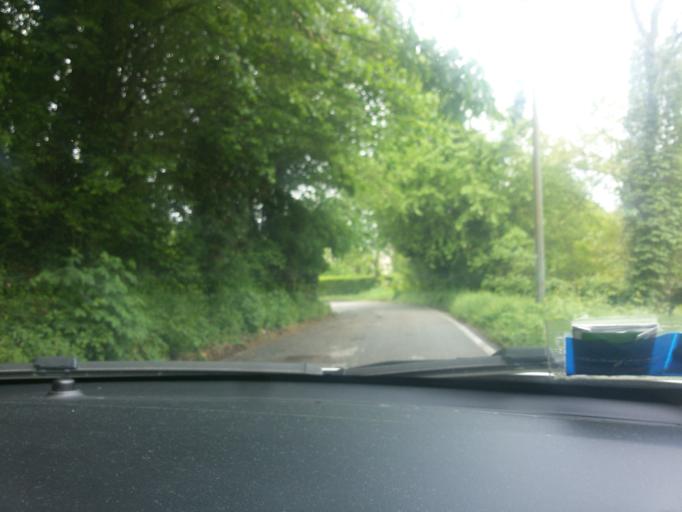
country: IT
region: Piedmont
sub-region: Provincia di Torino
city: Turin
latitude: 45.0486
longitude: 7.7002
